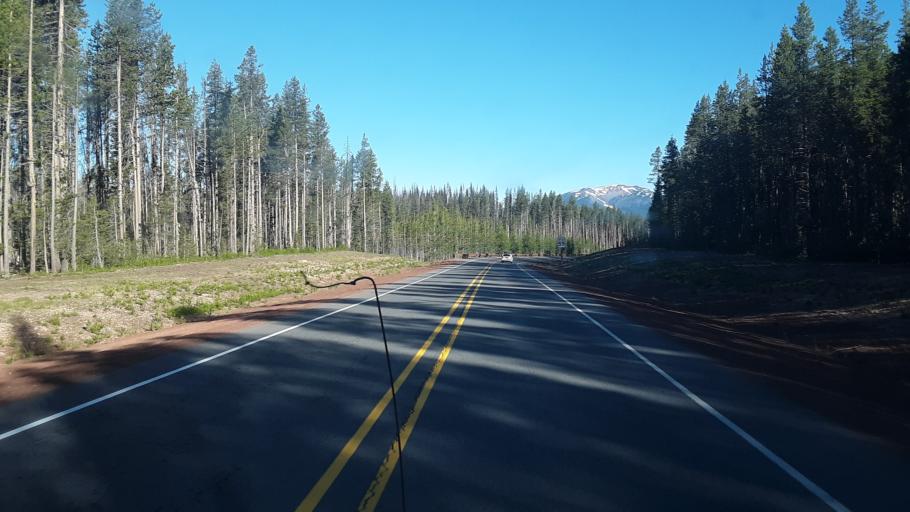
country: US
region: Oregon
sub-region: Lane County
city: Oakridge
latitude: 43.0896
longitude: -122.1183
